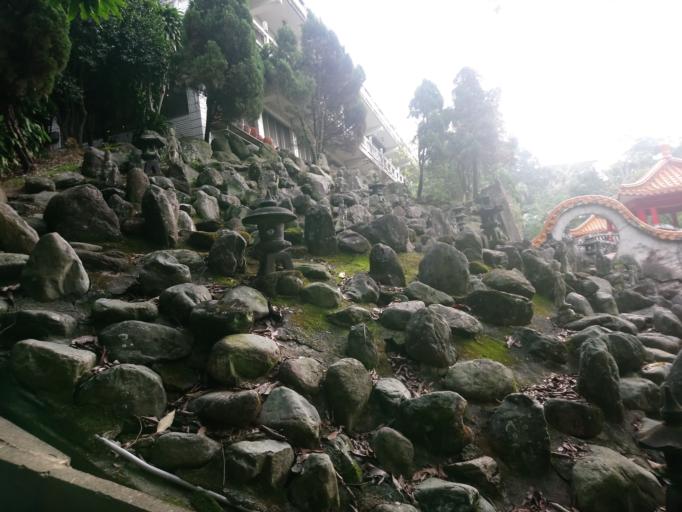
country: TW
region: Taiwan
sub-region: Hsinchu
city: Hsinchu
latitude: 24.7809
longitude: 120.9783
